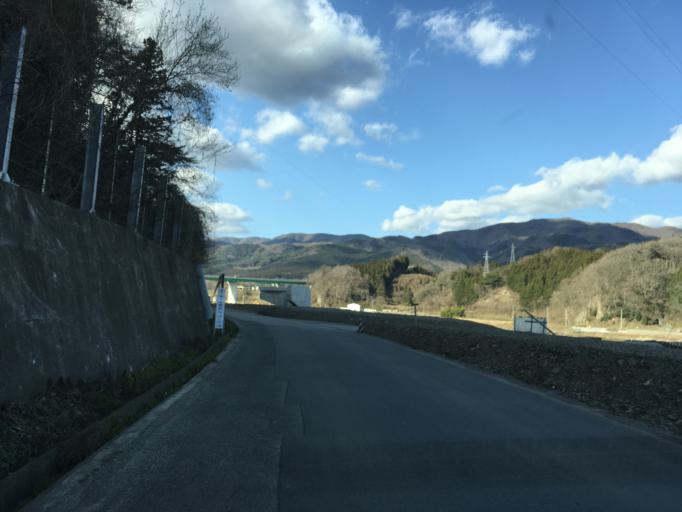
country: JP
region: Iwate
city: Ofunato
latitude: 39.0221
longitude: 141.6163
